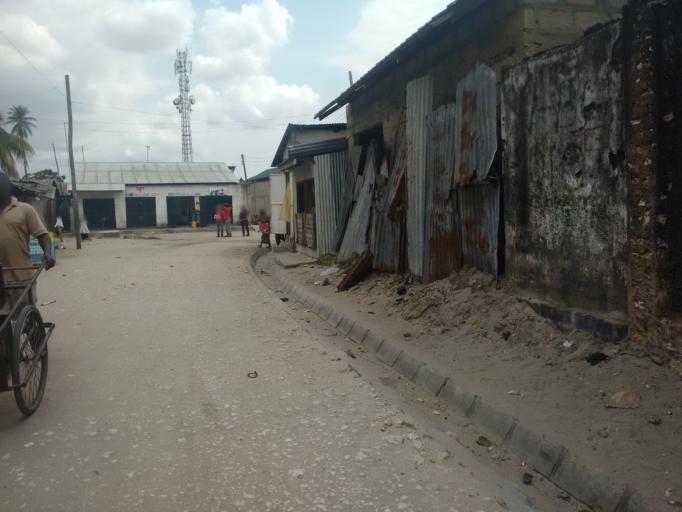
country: TZ
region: Dar es Salaam
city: Dar es Salaam
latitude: -6.8538
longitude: 39.2530
